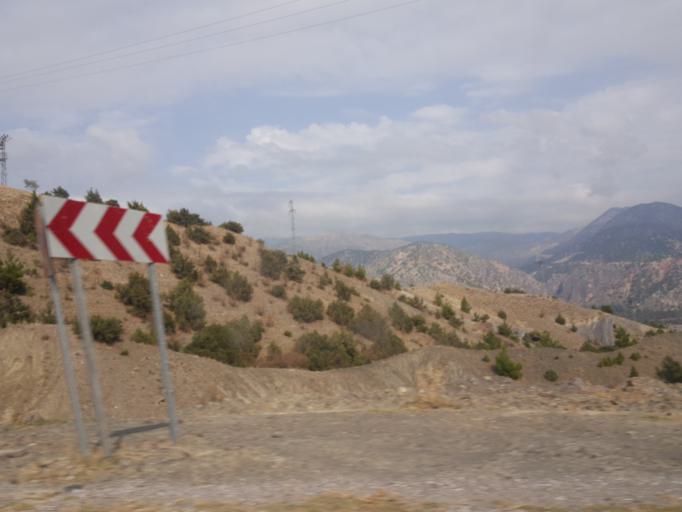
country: TR
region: Corum
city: Kamil
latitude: 41.1108
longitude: 34.7419
